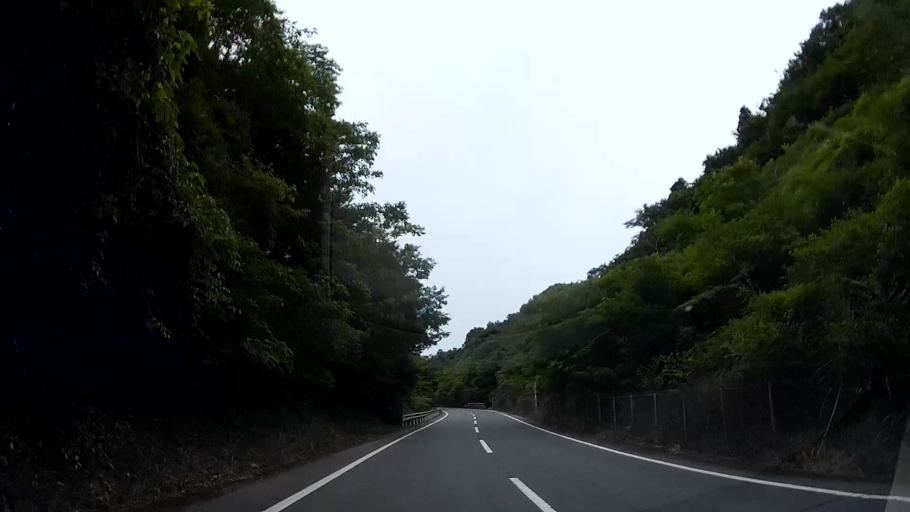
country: JP
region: Kumamoto
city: Kikuchi
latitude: 33.0599
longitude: 130.9049
